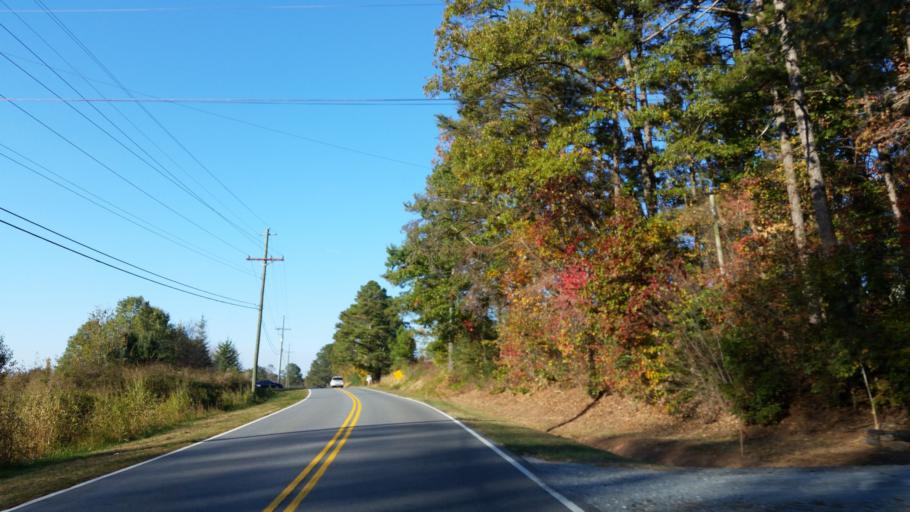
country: US
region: Georgia
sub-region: Gilmer County
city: Ellijay
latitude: 34.6478
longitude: -84.4694
